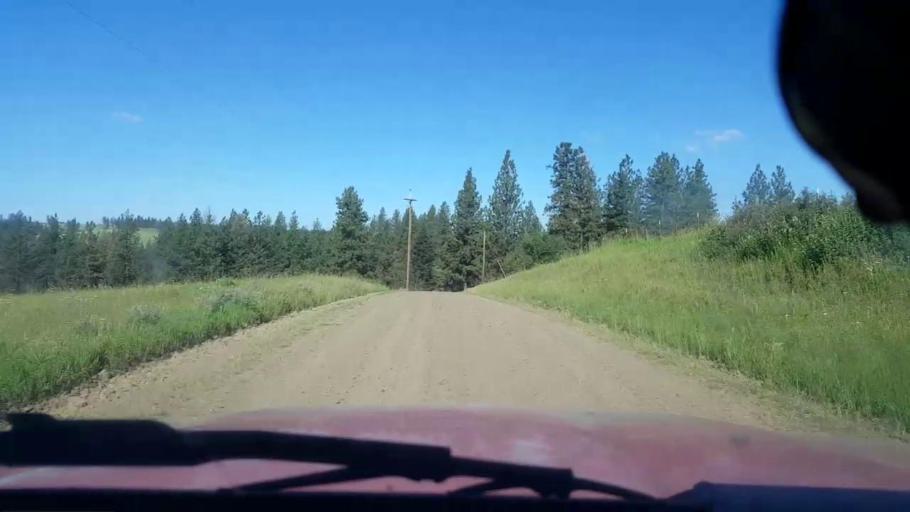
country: US
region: Washington
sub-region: Garfield County
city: Pomeroy
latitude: 45.9845
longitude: -117.4694
